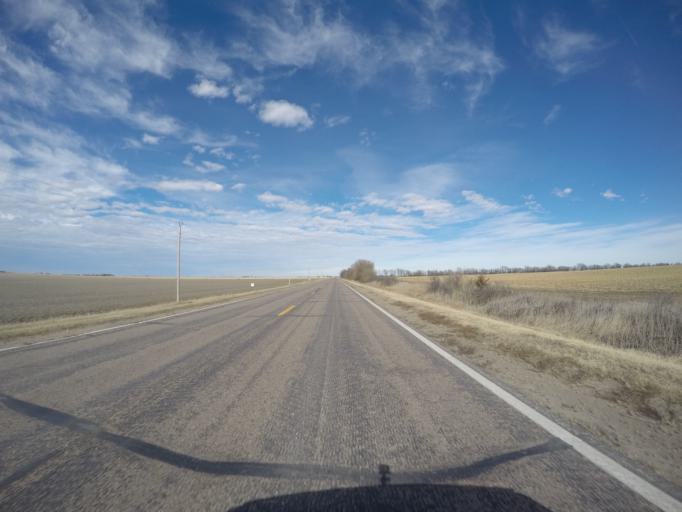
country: US
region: Nebraska
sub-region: Franklin County
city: Franklin
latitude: 40.2521
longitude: -98.9523
